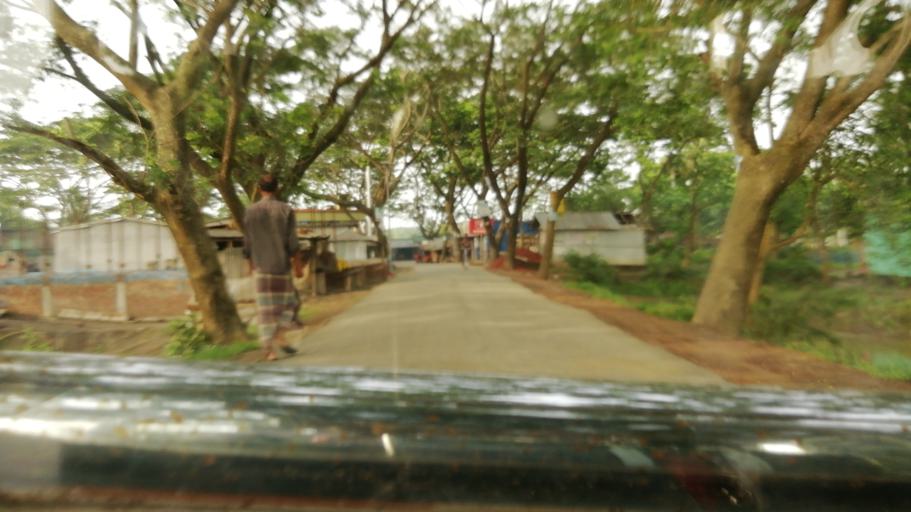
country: BD
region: Khulna
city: Bhatpara Abhaynagar
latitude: 23.0376
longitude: 89.3052
